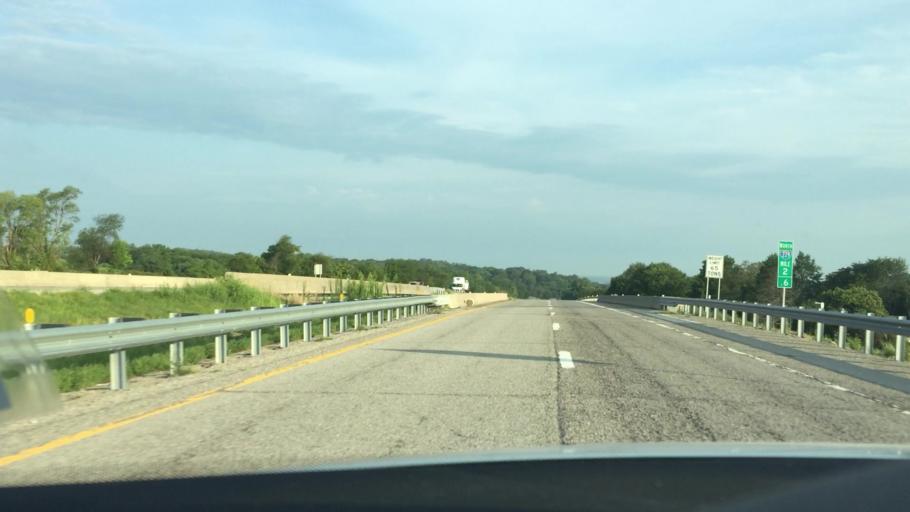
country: US
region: Missouri
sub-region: Buchanan County
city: Saint Joseph
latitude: 39.7215
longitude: -94.8333
